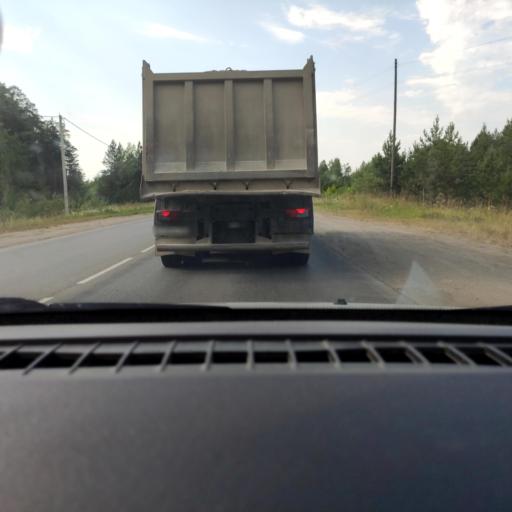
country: RU
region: Perm
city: Overyata
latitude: 58.0193
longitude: 55.8567
